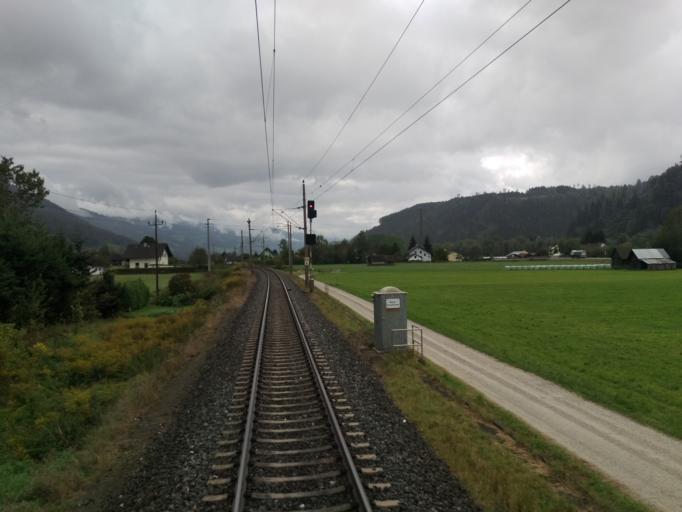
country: AT
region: Styria
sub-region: Politischer Bezirk Liezen
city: Oblarn
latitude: 47.4643
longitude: 13.9947
